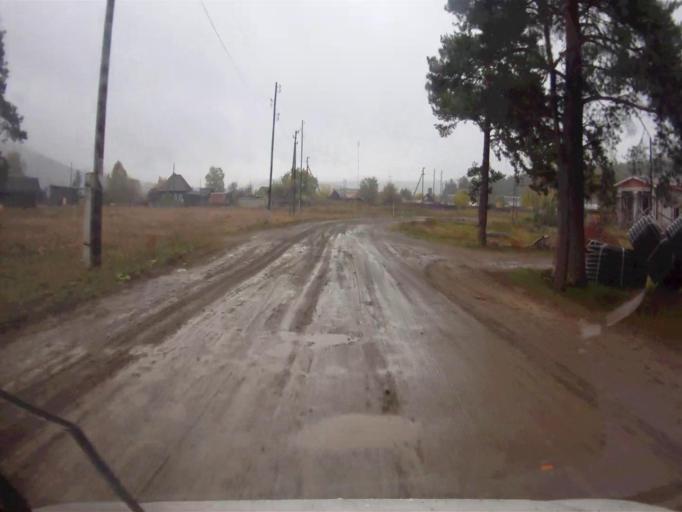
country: RU
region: Chelyabinsk
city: Kyshtym
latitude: 55.9015
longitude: 60.4656
